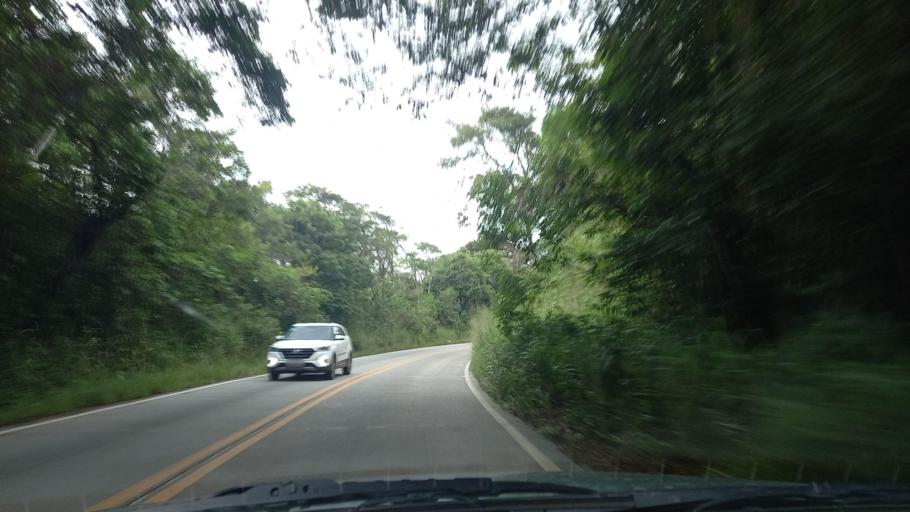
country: BR
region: Pernambuco
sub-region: Quipapa
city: Quipapa
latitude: -8.7904
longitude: -35.9929
